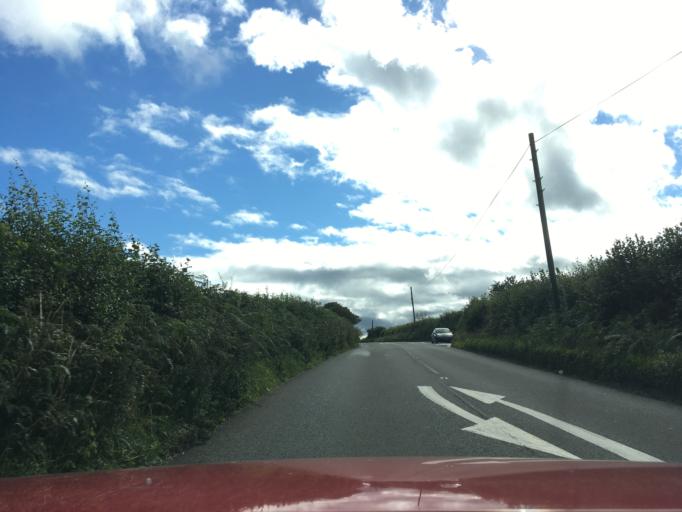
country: GB
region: England
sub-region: Devon
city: Kingsbridge
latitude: 50.3485
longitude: -3.7293
